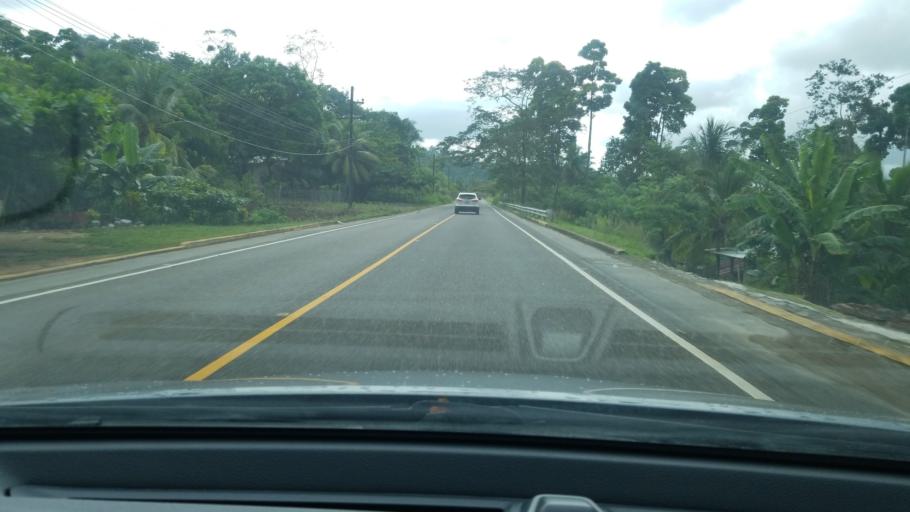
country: HN
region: Cortes
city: Potrerillos
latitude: 15.6108
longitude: -88.2856
